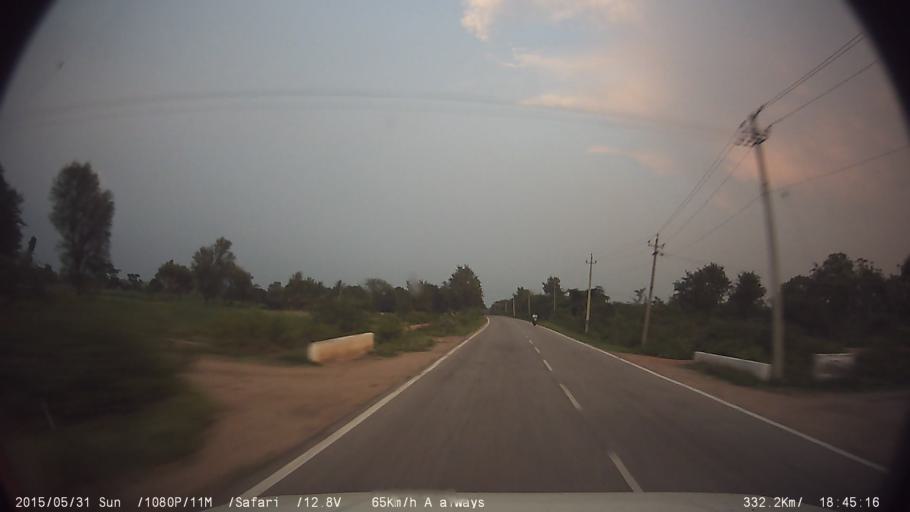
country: IN
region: Karnataka
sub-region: Mysore
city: Tirumakudal Narsipur
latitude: 12.1588
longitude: 76.8229
